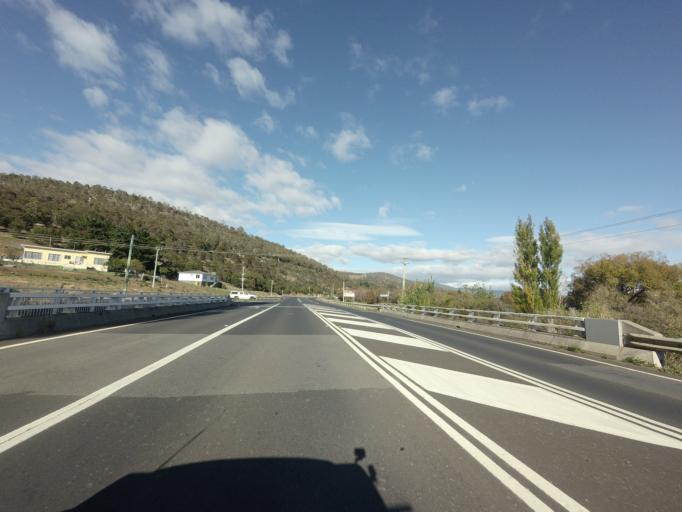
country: AU
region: Tasmania
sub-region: Derwent Valley
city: New Norfolk
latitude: -42.7819
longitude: 147.1085
